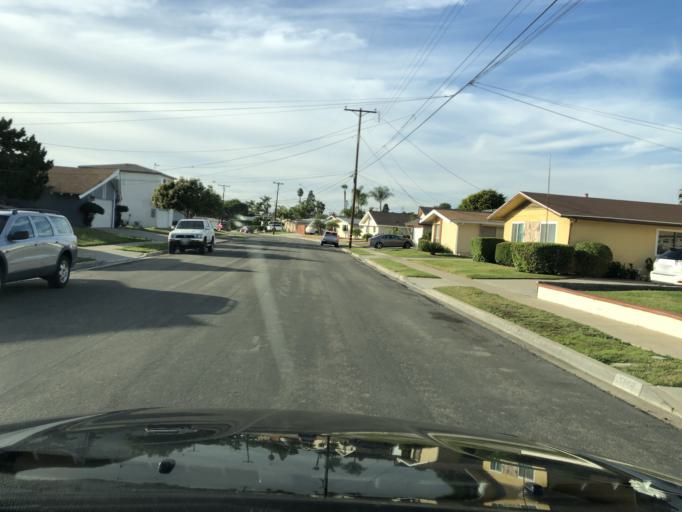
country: US
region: California
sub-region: San Diego County
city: La Jolla
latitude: 32.8260
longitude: -117.1746
